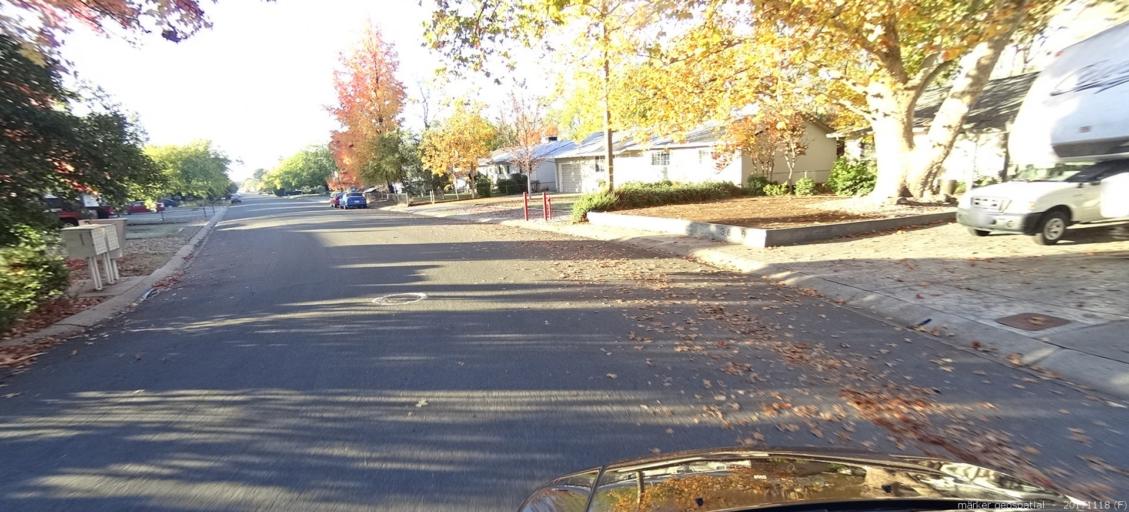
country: US
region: California
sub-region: Shasta County
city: Cottonwood
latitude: 40.3936
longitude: -122.2903
